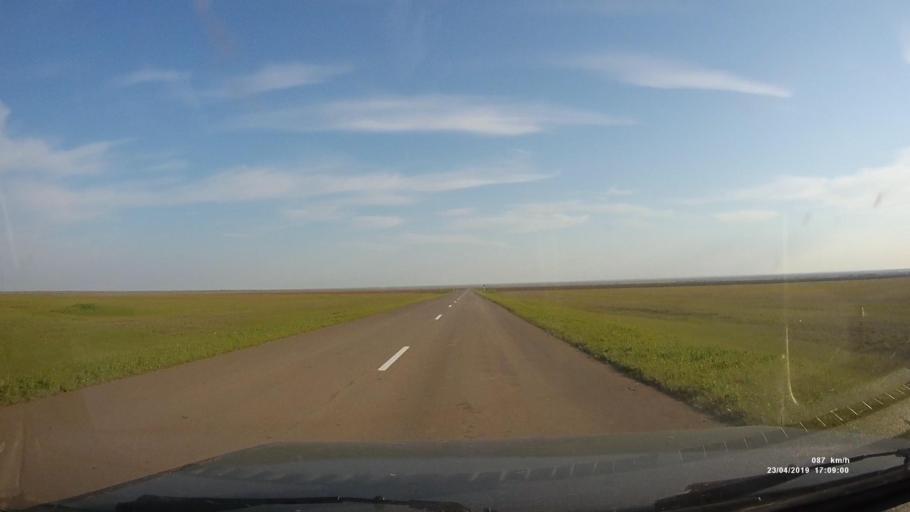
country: RU
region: Kalmykiya
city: Priyutnoye
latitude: 46.2645
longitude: 43.4843
